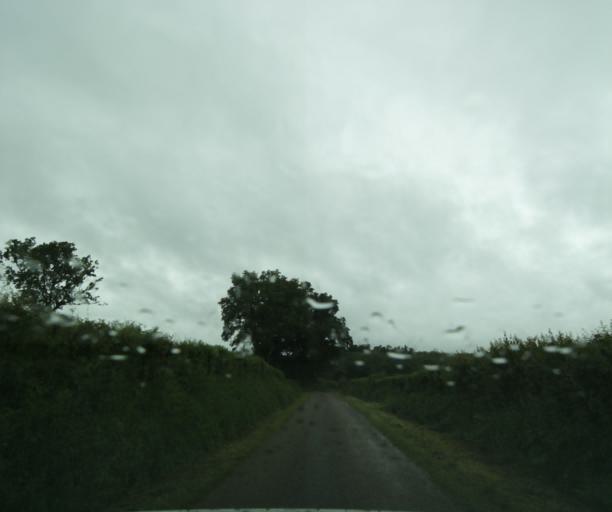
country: FR
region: Bourgogne
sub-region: Departement de Saone-et-Loire
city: Charolles
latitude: 46.4691
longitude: 4.2928
